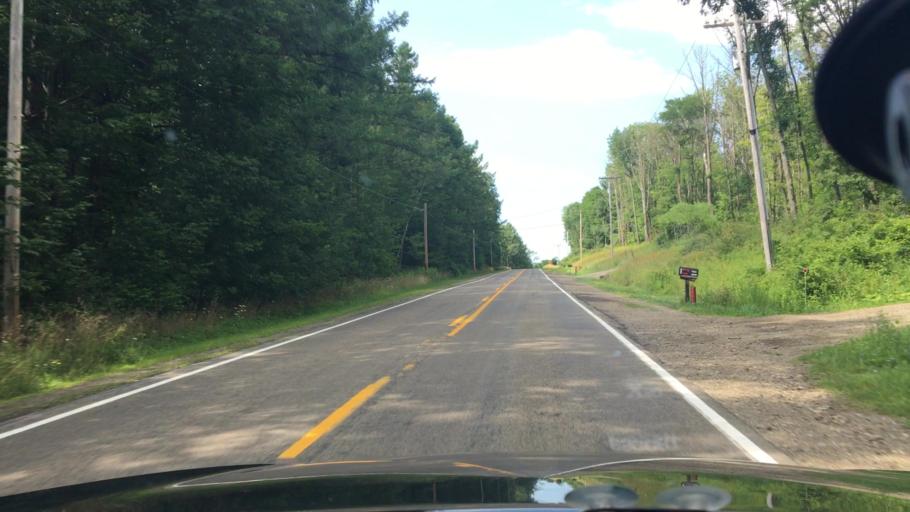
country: US
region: New York
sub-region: Chautauqua County
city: Lakewood
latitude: 42.2235
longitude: -79.3616
